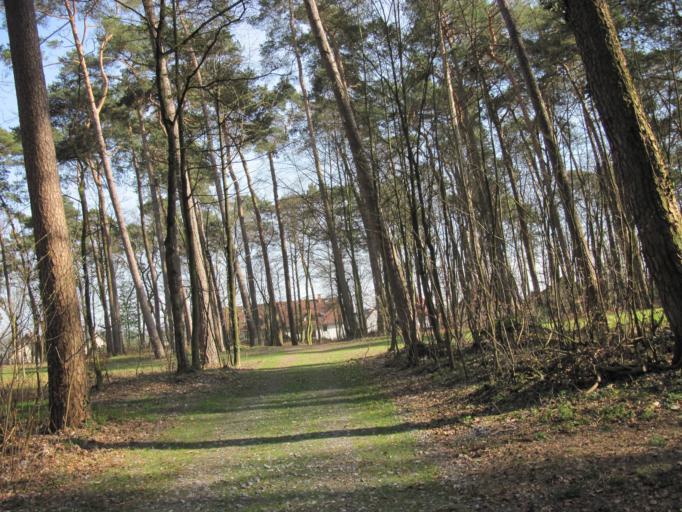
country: DE
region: North Rhine-Westphalia
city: Bad Lippspringe
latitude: 51.7913
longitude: 8.8193
